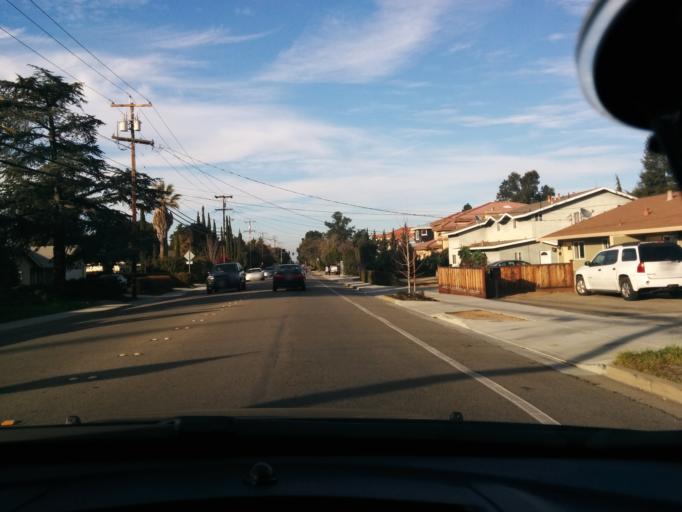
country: US
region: California
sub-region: Santa Clara County
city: Cupertino
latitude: 37.3284
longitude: -122.0414
